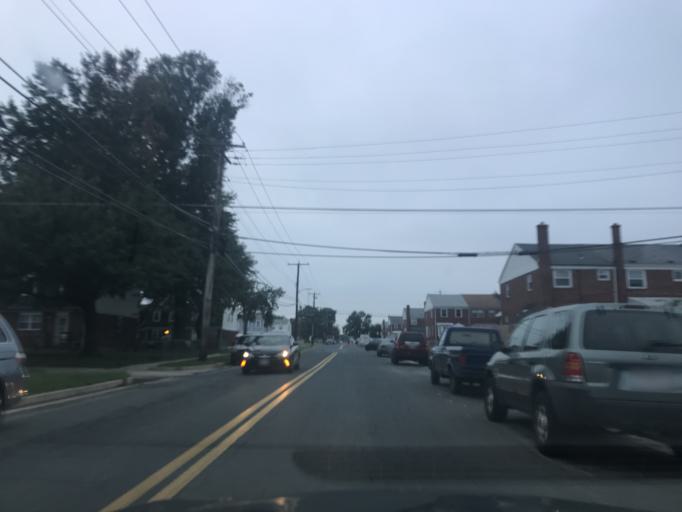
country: US
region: Maryland
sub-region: Baltimore County
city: Dundalk
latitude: 39.2605
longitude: -76.4912
